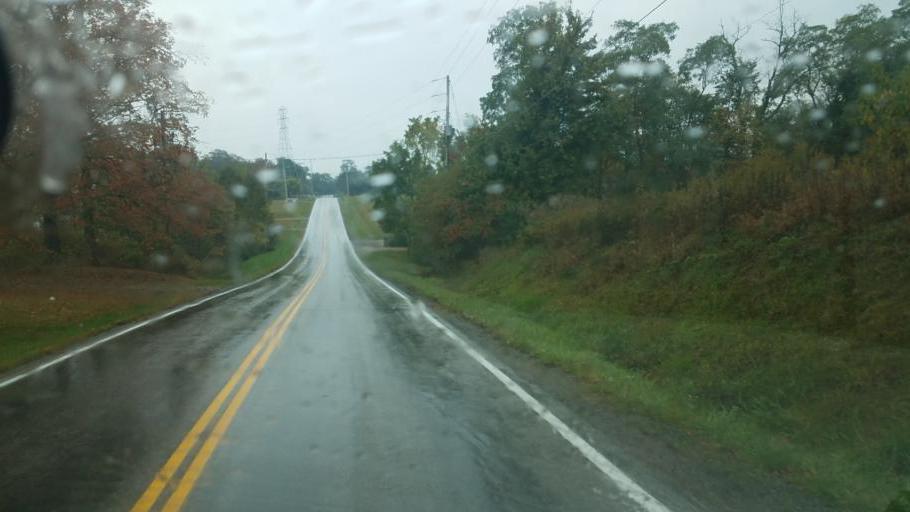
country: US
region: Ohio
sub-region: Ashland County
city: Ashland
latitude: 40.8323
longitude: -82.3336
